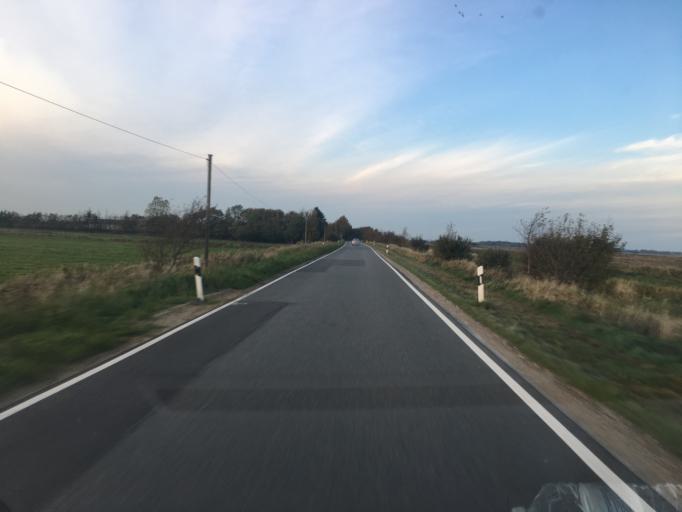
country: DE
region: Schleswig-Holstein
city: Humptrup
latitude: 54.8909
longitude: 8.8485
